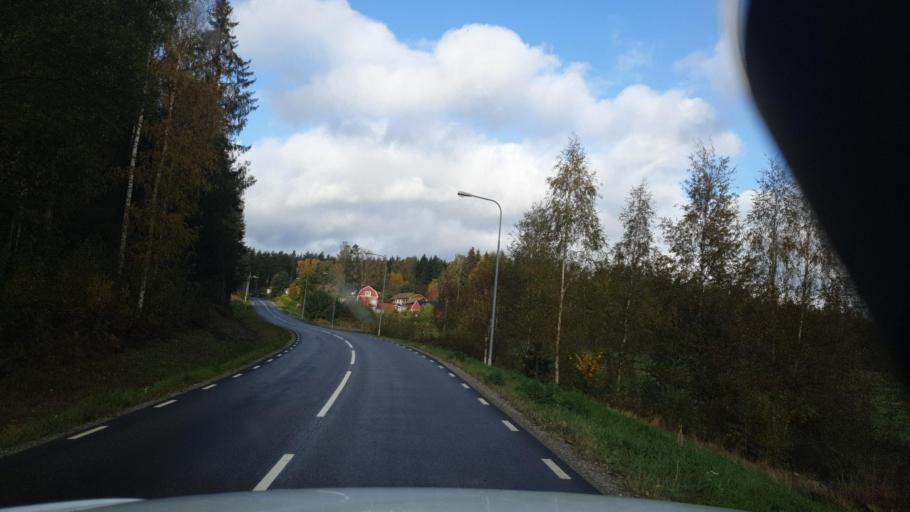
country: SE
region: Vaermland
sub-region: Arvika Kommun
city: Arvika
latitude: 59.5367
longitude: 12.5943
